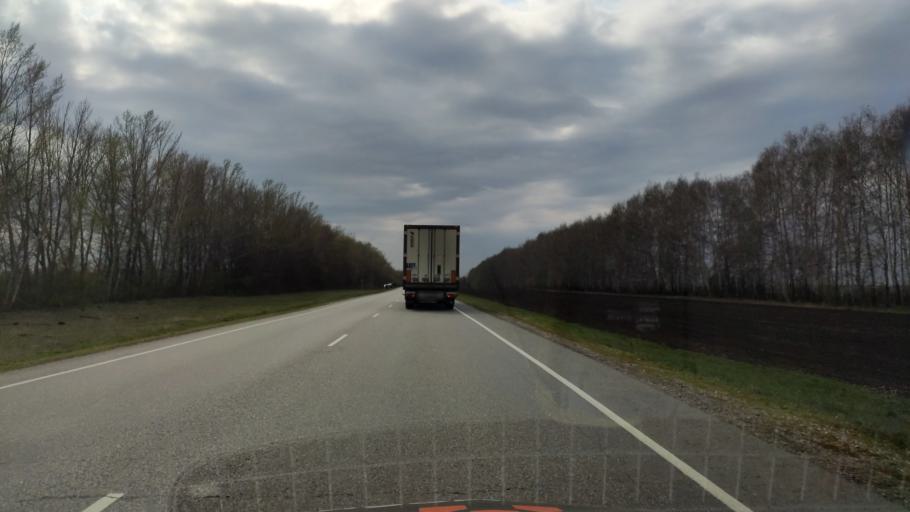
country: RU
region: Voronezj
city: Nizhnedevitsk
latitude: 51.5561
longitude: 38.2313
